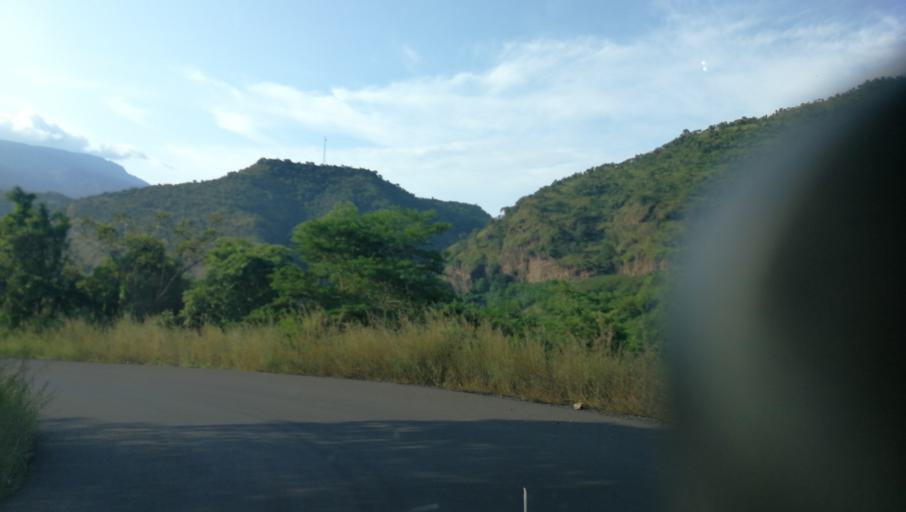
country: ET
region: Southern Nations, Nationalities, and People's Region
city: Areka
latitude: 6.8285
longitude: 37.2974
